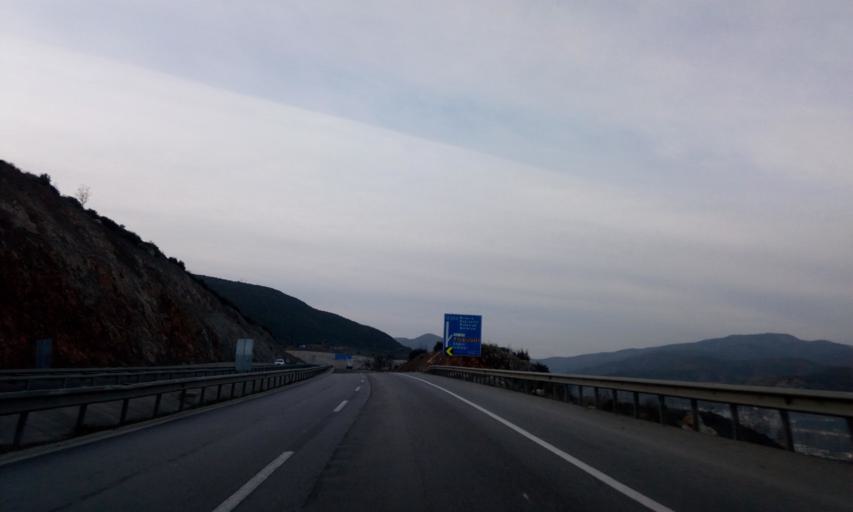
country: TR
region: Bilecik
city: Kuplu
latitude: 40.1280
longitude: 30.0154
